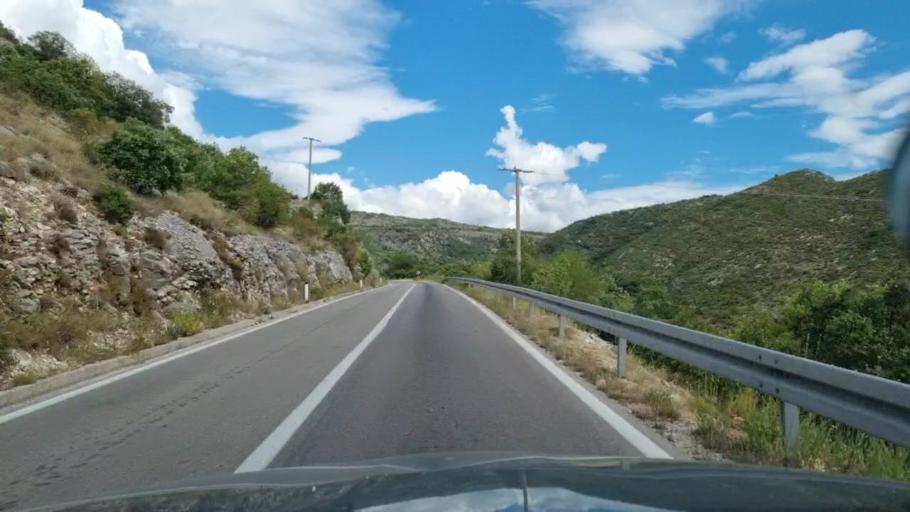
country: BA
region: Federation of Bosnia and Herzegovina
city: Blagaj
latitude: 43.2625
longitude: 17.9167
